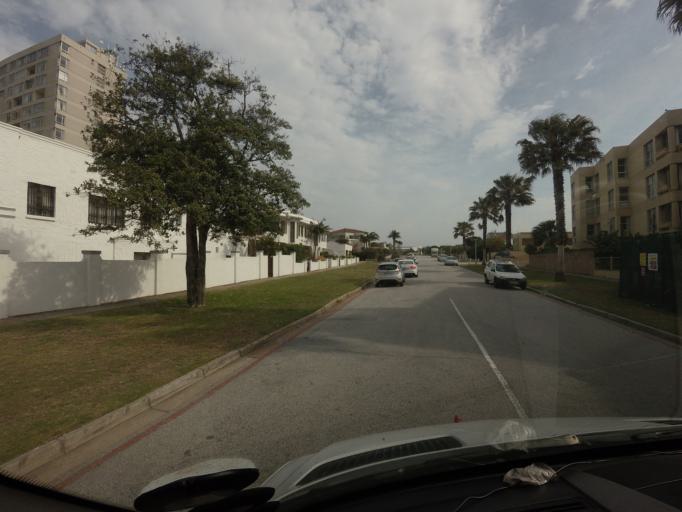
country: ZA
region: Eastern Cape
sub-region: Nelson Mandela Bay Metropolitan Municipality
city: Port Elizabeth
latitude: -33.9822
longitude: 25.6605
